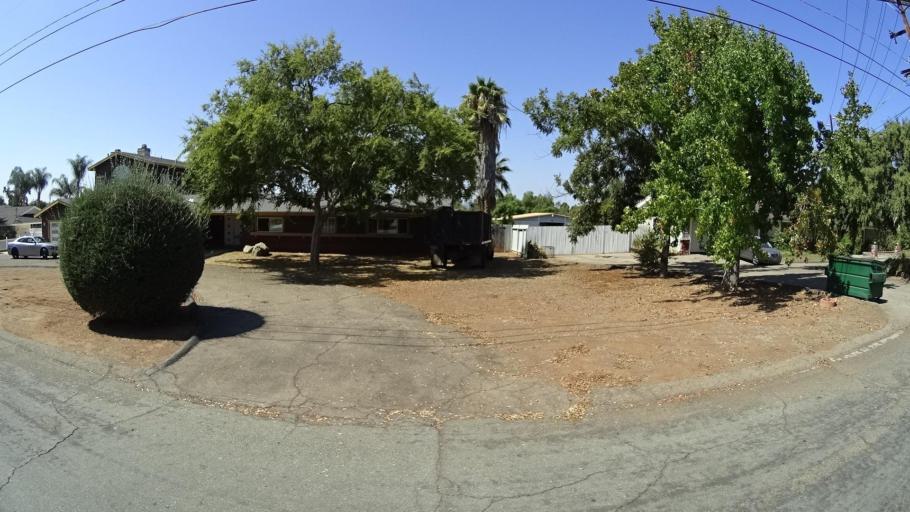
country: US
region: California
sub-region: San Diego County
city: Granite Hills
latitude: 32.8024
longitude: -116.9121
